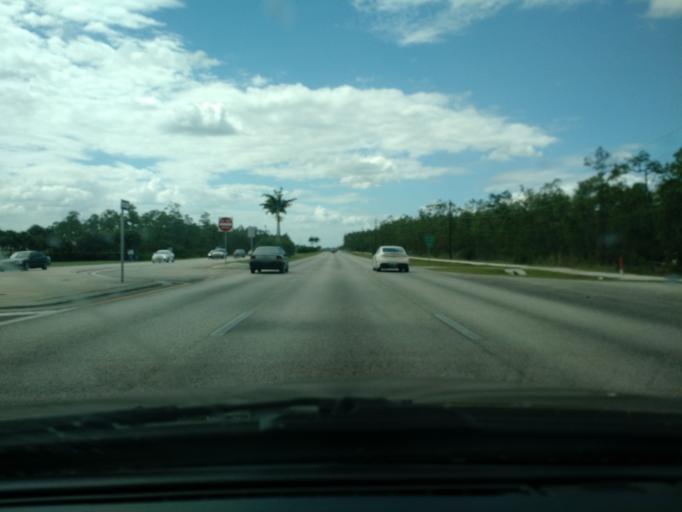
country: US
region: Florida
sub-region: Lee County
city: Gateway
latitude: 26.6131
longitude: -81.7859
